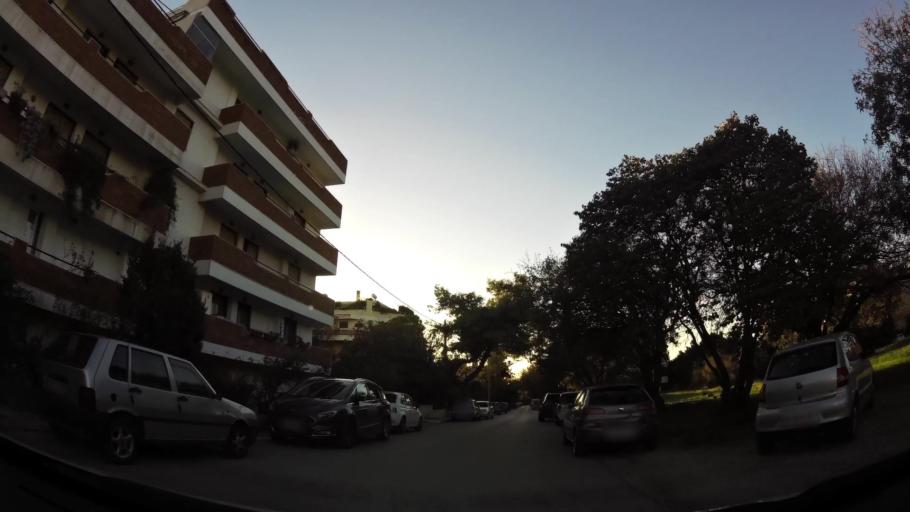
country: GR
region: Attica
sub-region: Nomarchia Athinas
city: Kifisia
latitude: 38.0730
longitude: 23.8039
